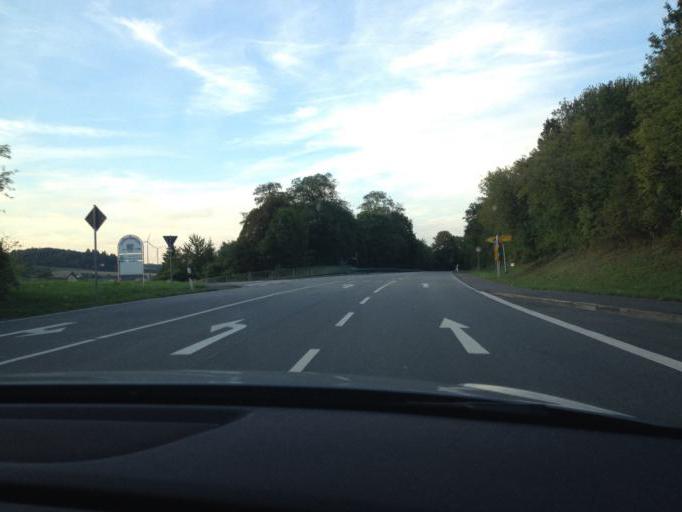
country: DE
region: Rheinland-Pfalz
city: Breitenbach
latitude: 49.4452
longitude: 7.2320
